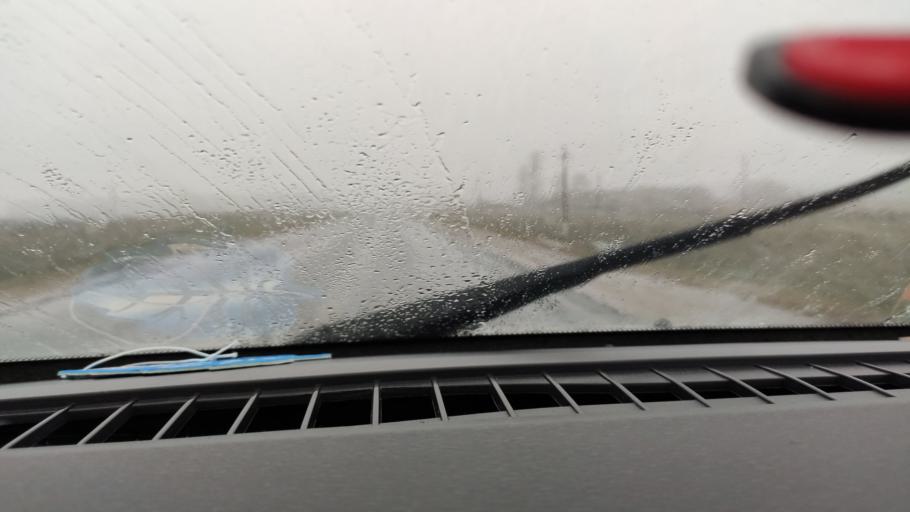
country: RU
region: Tatarstan
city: Cheremshan
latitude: 54.7205
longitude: 51.2534
